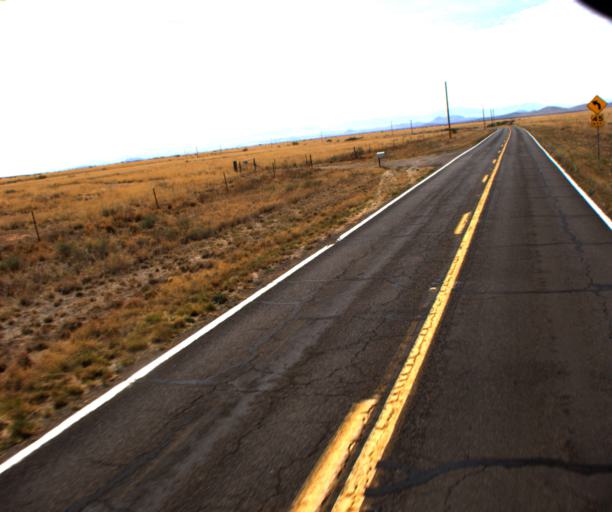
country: US
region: Arizona
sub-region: Cochise County
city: Willcox
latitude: 31.9923
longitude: -109.4449
